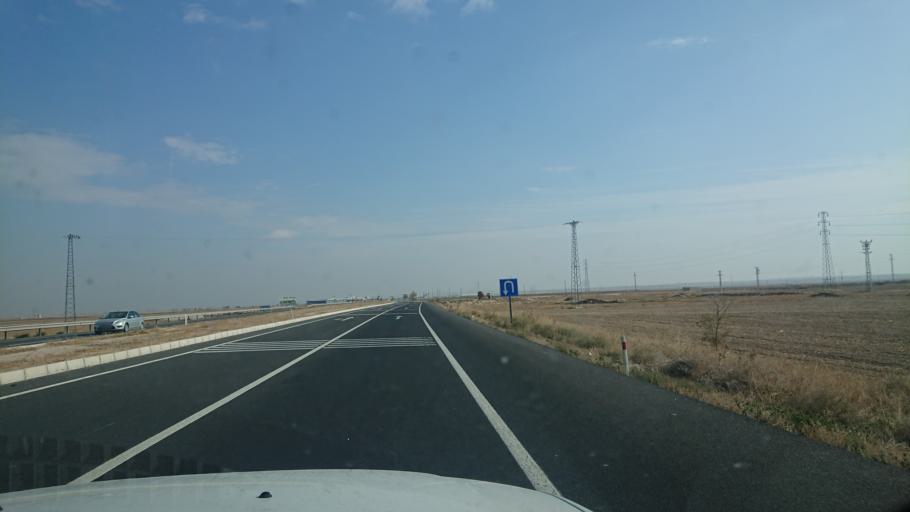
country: TR
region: Aksaray
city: Yesilova
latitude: 38.3103
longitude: 33.8300
